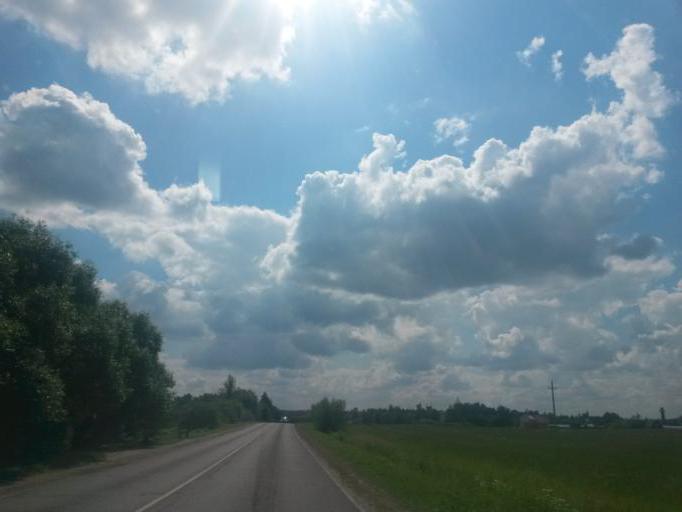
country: RU
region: Moskovskaya
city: Belyye Stolby
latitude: 55.2897
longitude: 37.7841
